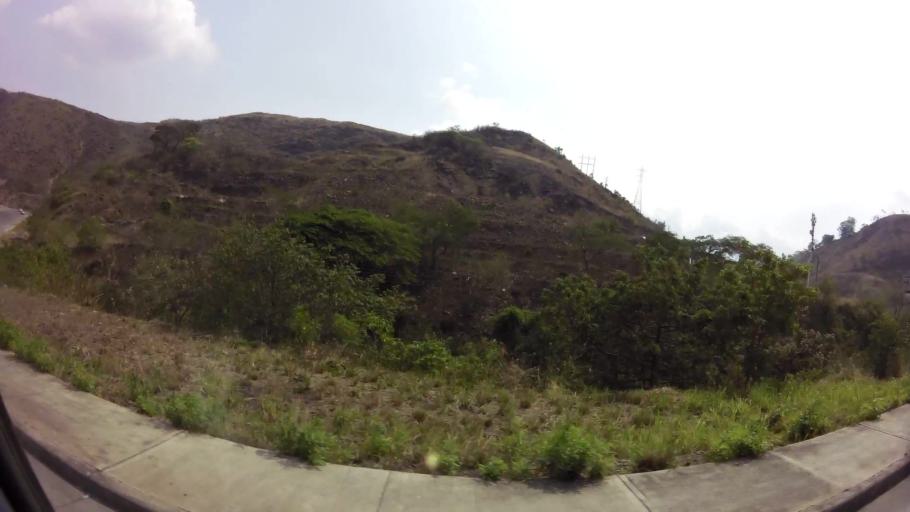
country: HN
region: Francisco Morazan
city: Tegucigalpa
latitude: 14.1162
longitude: -87.2167
